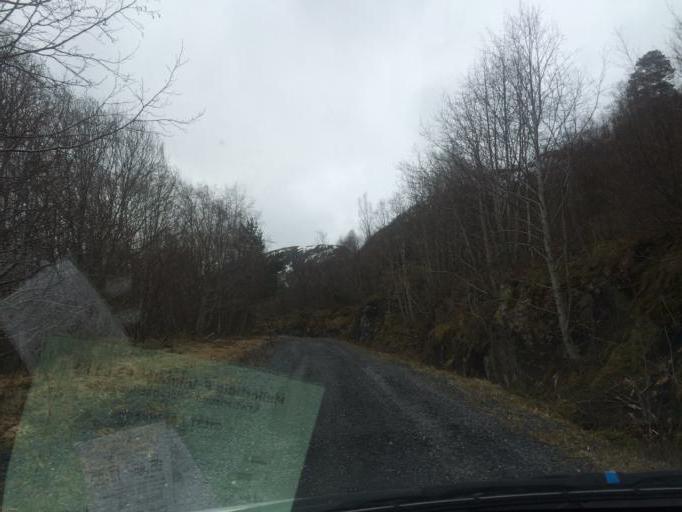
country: NO
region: More og Romsdal
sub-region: Gjemnes
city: Batnfjordsora
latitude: 62.9658
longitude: 7.7304
